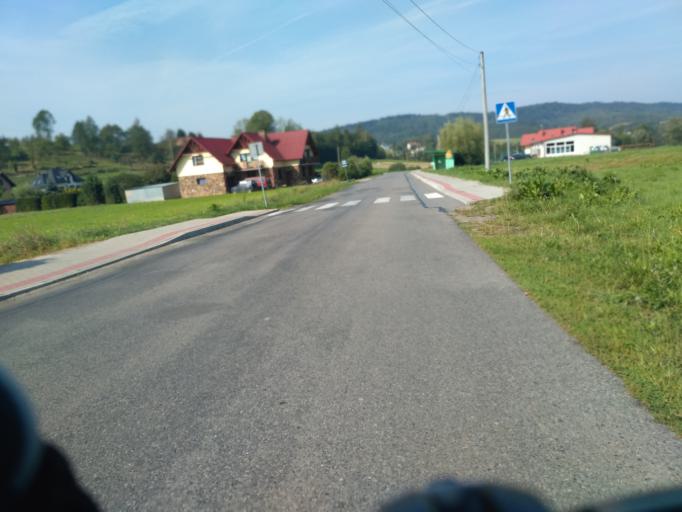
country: PL
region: Subcarpathian Voivodeship
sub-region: Powiat brzozowski
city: Golcowa
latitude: 49.7745
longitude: 22.0132
